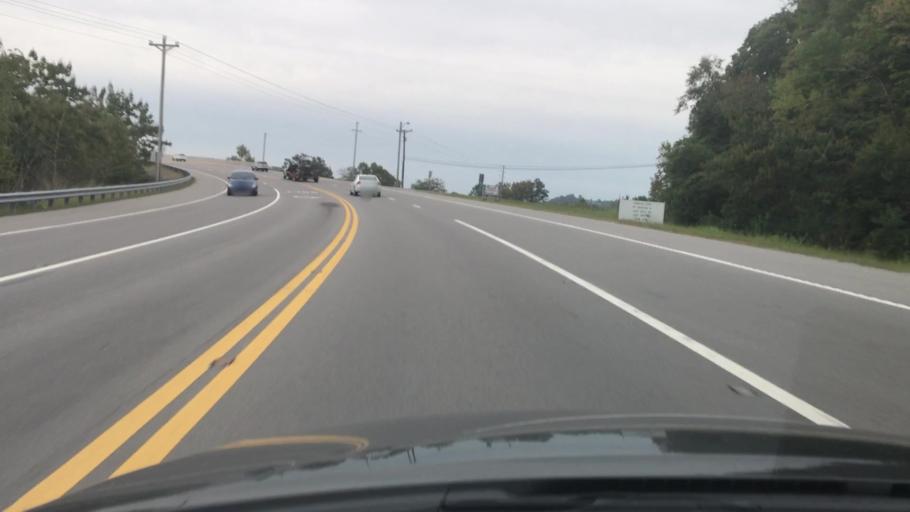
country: US
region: Tennessee
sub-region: Cheatham County
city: Ashland City
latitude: 36.2705
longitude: -87.0803
